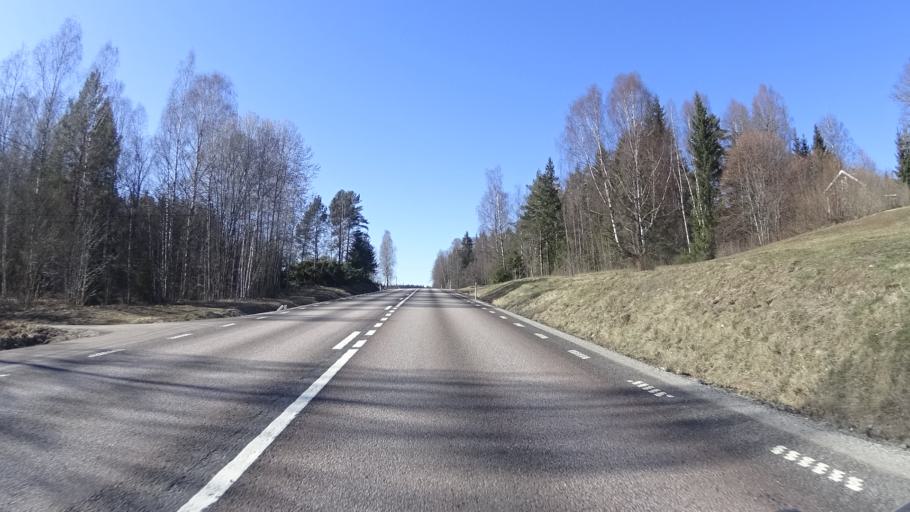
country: SE
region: Vaermland
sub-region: Sunne Kommun
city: Sunne
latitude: 59.6639
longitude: 12.9196
